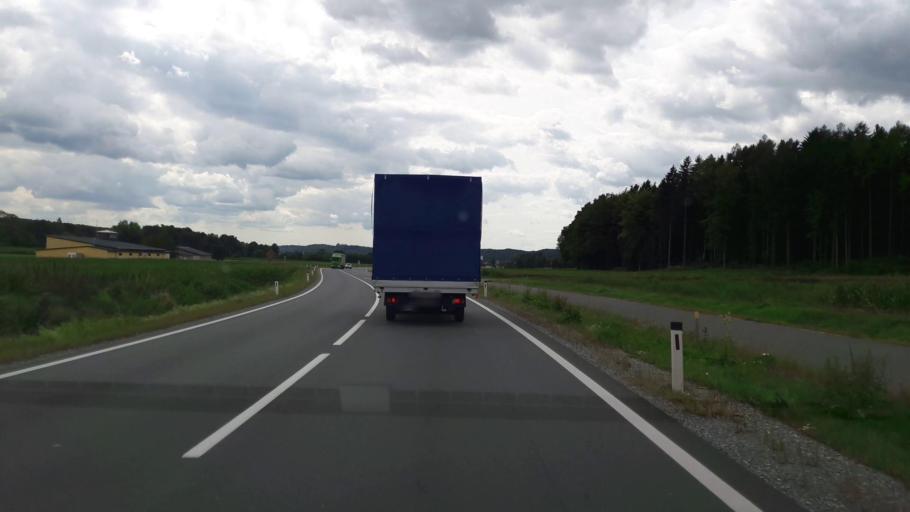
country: AT
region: Styria
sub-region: Politischer Bezirk Weiz
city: Unterfladnitz
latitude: 47.1725
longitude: 15.6620
